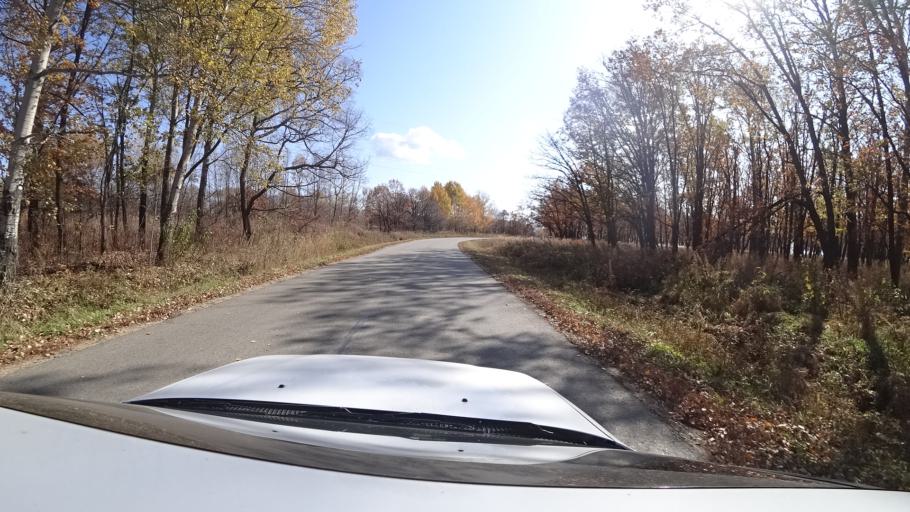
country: RU
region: Primorskiy
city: Lazo
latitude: 45.8704
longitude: 133.6597
